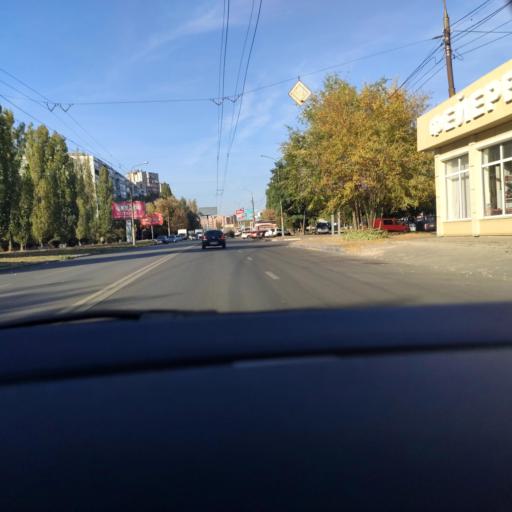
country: RU
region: Voronezj
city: Podgornoye
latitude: 51.7024
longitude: 39.1484
